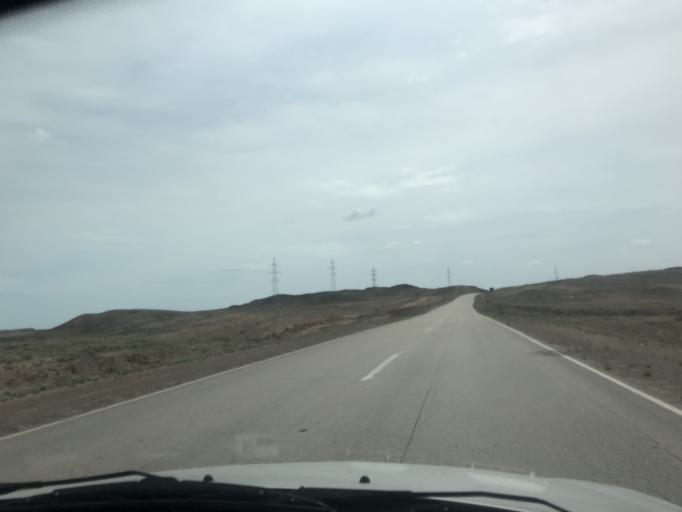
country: KZ
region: Zhambyl
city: Mynaral
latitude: 45.3567
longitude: 73.6797
